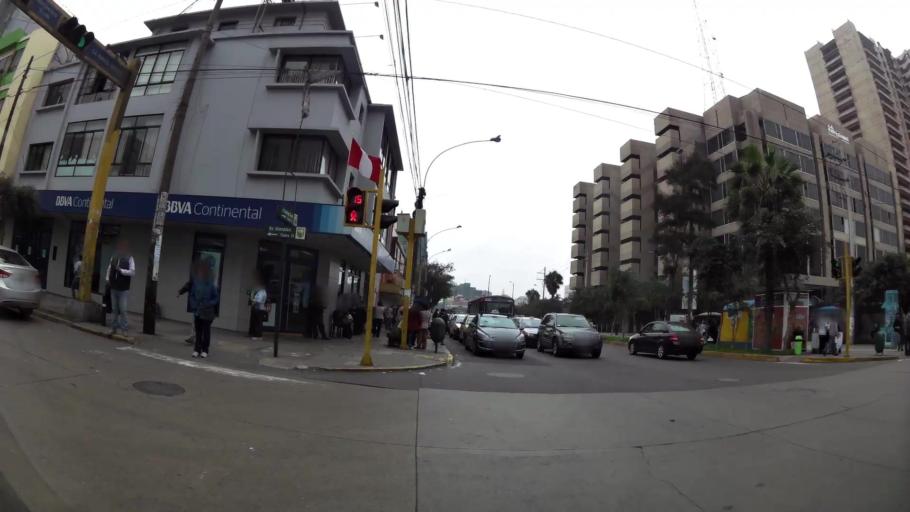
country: PE
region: Lima
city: Lima
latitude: -12.0800
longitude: -77.0362
